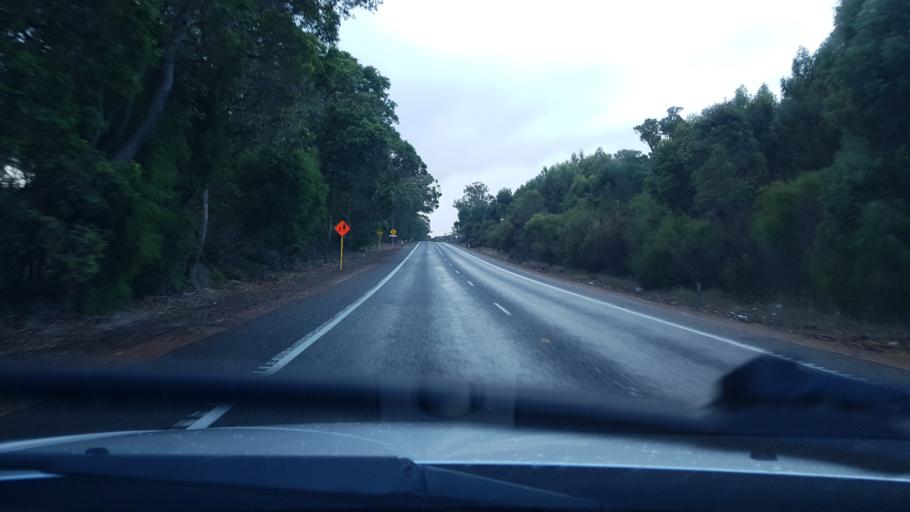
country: AU
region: Western Australia
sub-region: Augusta-Margaret River Shire
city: Margaret River
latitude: -33.8861
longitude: 115.0875
